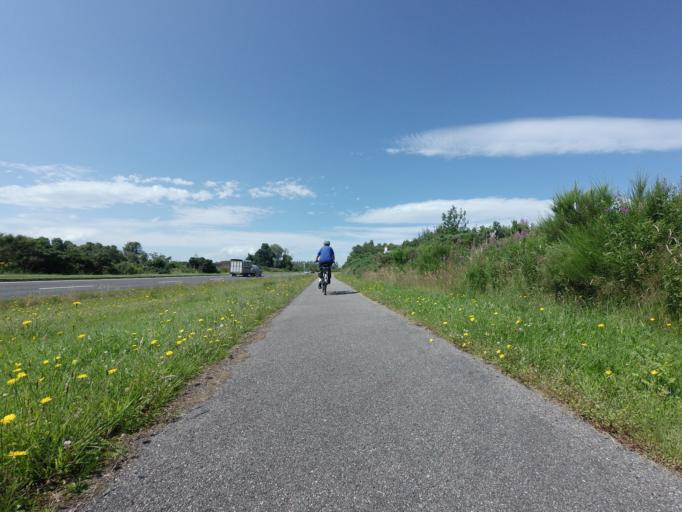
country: GB
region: Scotland
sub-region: Highland
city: Conon Bridge
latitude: 57.5388
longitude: -4.3681
